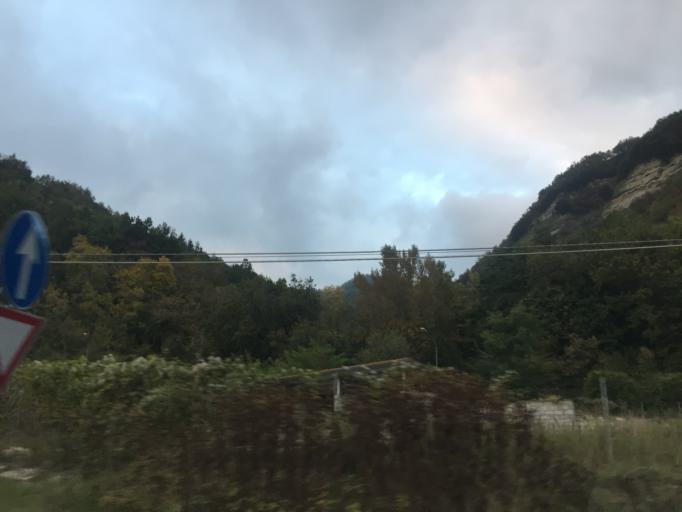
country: IT
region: The Marches
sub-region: Provincia di Ascoli Piceno
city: Arquata del Tronto
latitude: 42.7750
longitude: 13.3084
